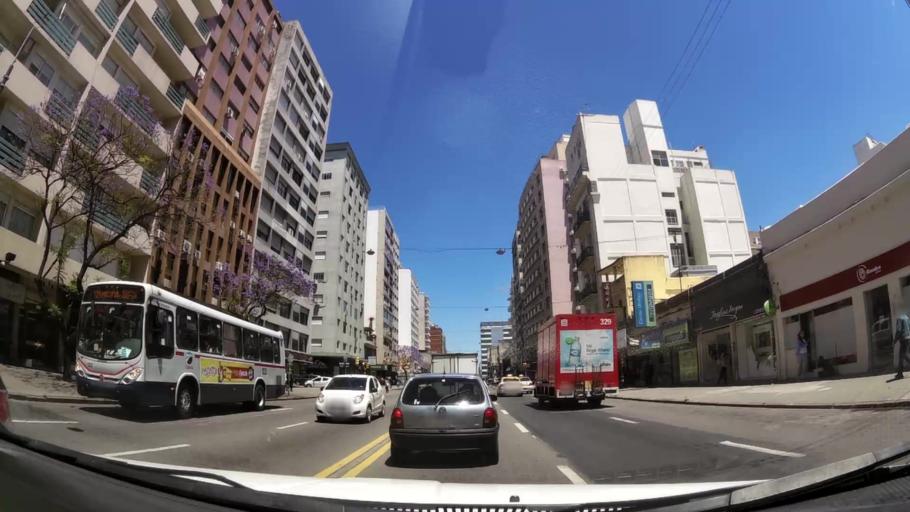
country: UY
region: Montevideo
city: Montevideo
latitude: -34.8996
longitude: -56.1704
